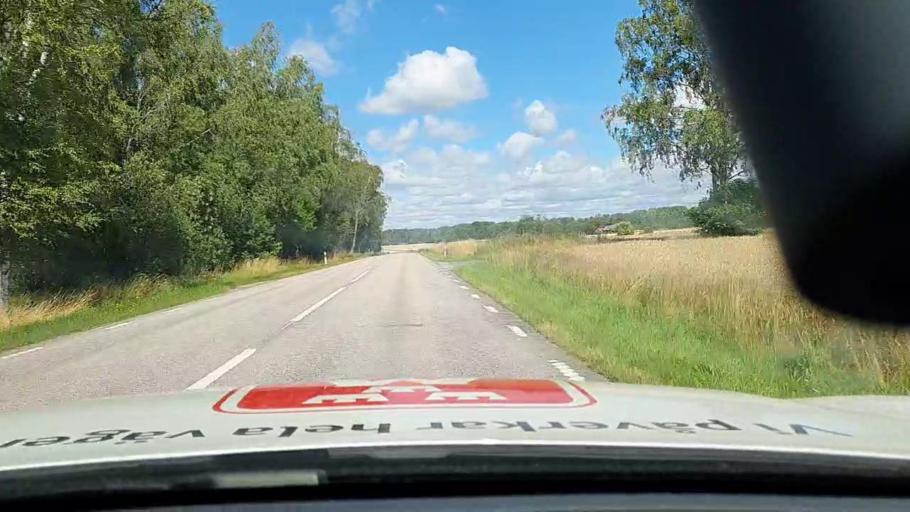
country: SE
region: Vaestra Goetaland
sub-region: Skovde Kommun
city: Stopen
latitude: 58.4898
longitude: 13.9617
